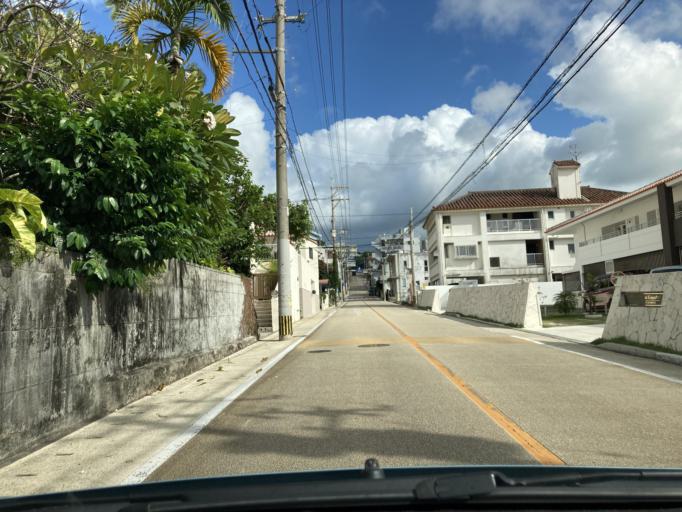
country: JP
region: Okinawa
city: Naha-shi
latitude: 26.2167
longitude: 127.7147
